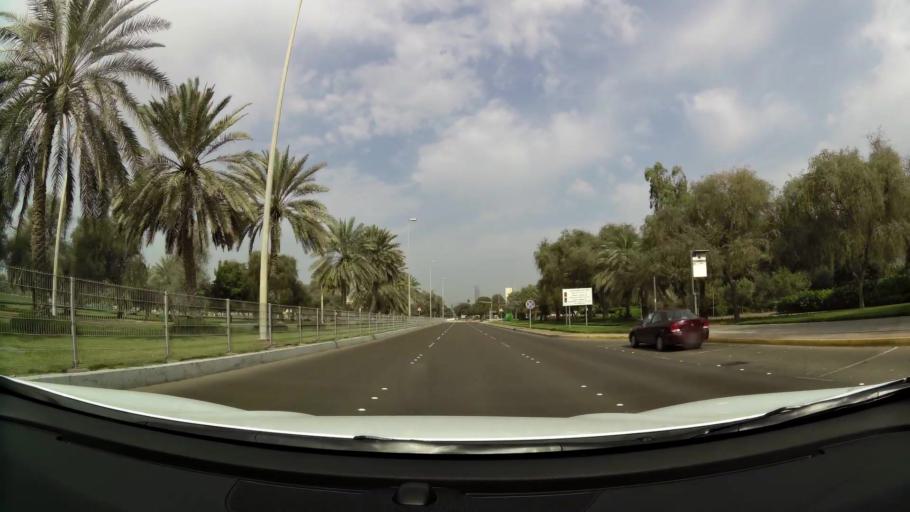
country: AE
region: Abu Dhabi
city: Abu Dhabi
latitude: 24.4526
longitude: 54.3787
